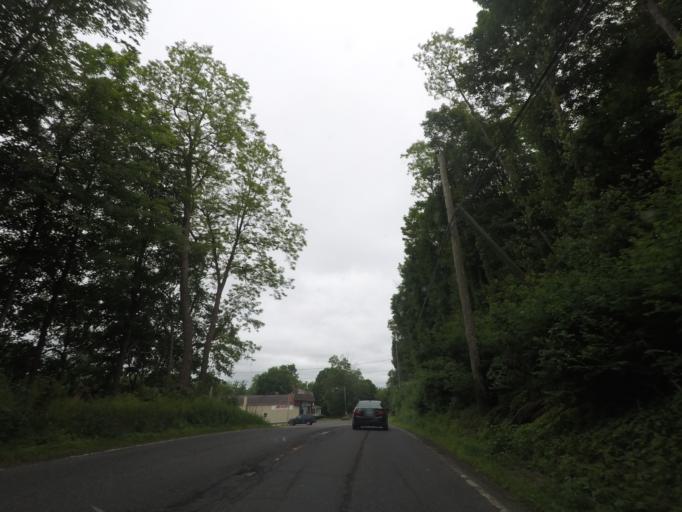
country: US
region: Connecticut
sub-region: Litchfield County
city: Canaan
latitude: 41.9555
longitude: -73.4773
